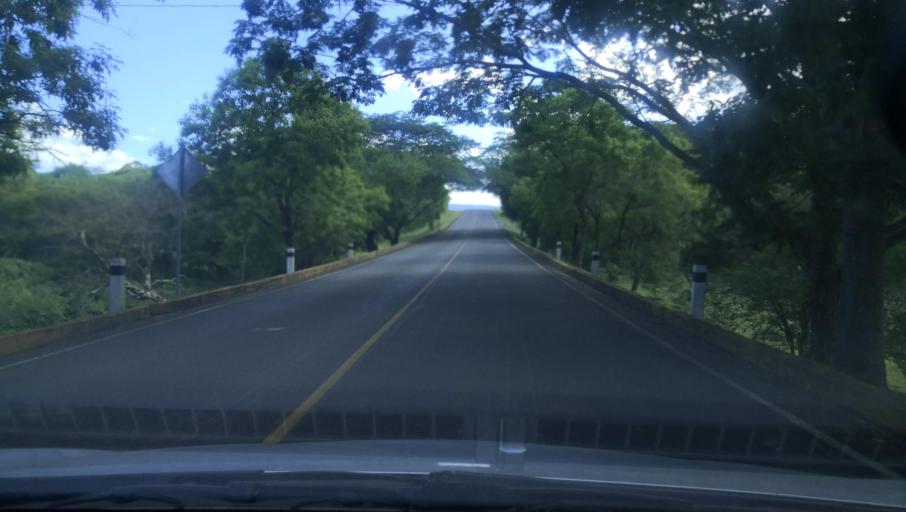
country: NI
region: Madriz
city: Somoto
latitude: 13.4638
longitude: -86.6587
